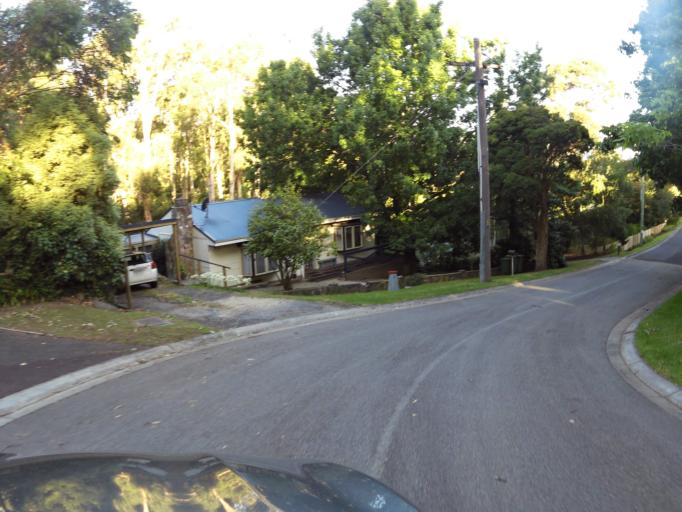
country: AU
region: Victoria
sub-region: Yarra Ranges
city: Tremont
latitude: -37.8992
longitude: 145.3289
